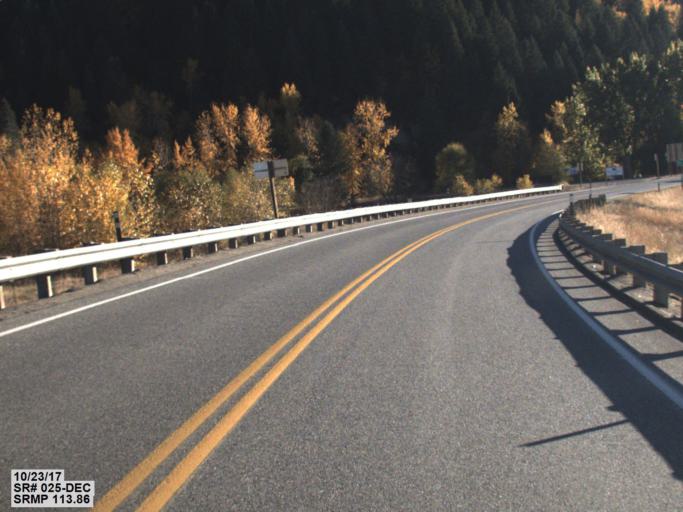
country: CA
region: British Columbia
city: Rossland
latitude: 48.9192
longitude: -117.7762
